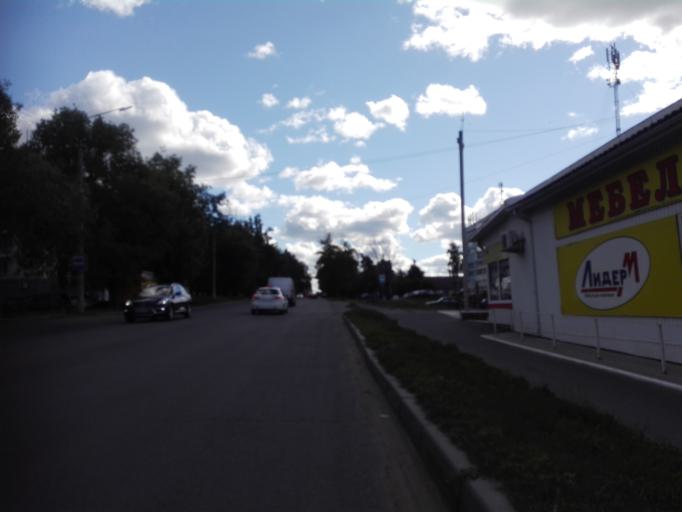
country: RU
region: Orjol
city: Orel
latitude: 52.9515
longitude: 36.0424
